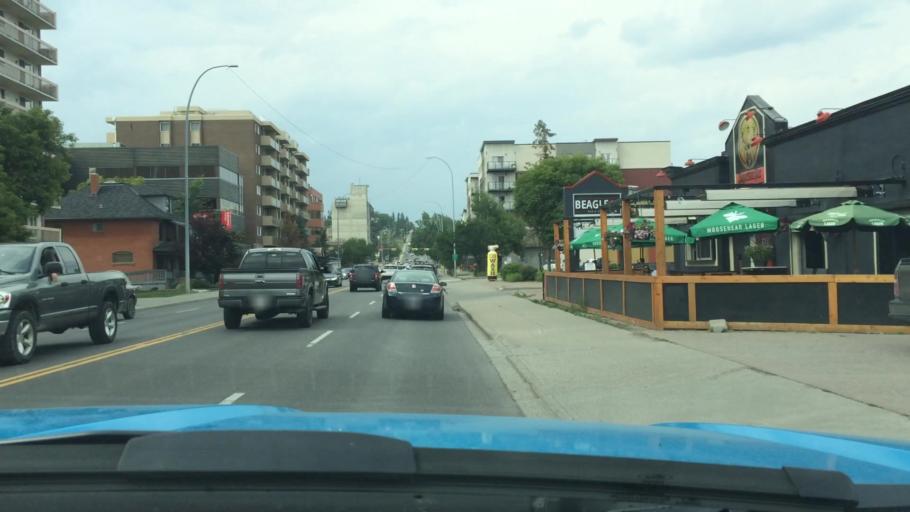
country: CA
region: Alberta
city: Calgary
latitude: 51.0553
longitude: -114.0947
